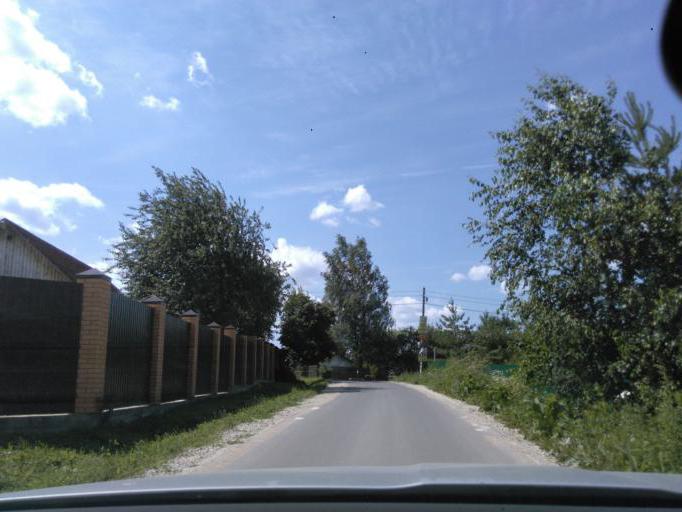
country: RU
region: Moskovskaya
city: Solnechnogorsk
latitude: 56.1312
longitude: 36.9651
